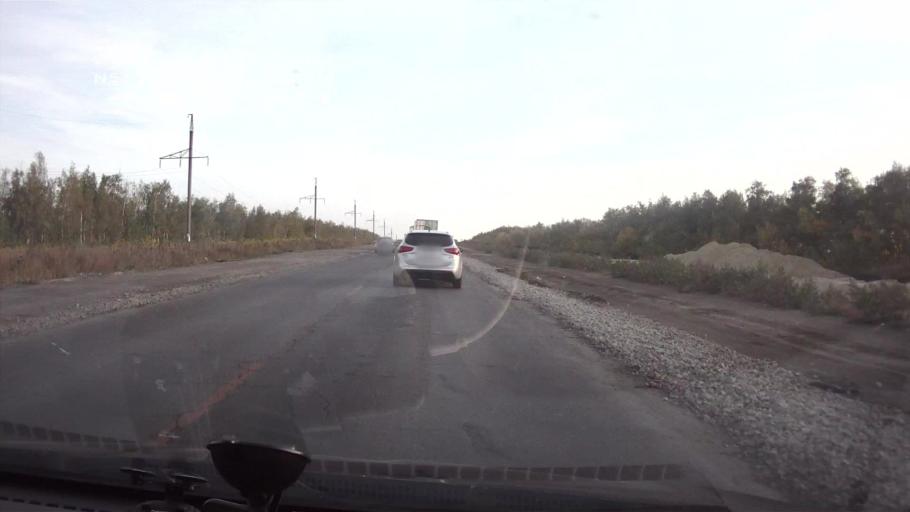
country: RU
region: Saratov
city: Krasnoarmeysk
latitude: 51.2378
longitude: 45.6461
